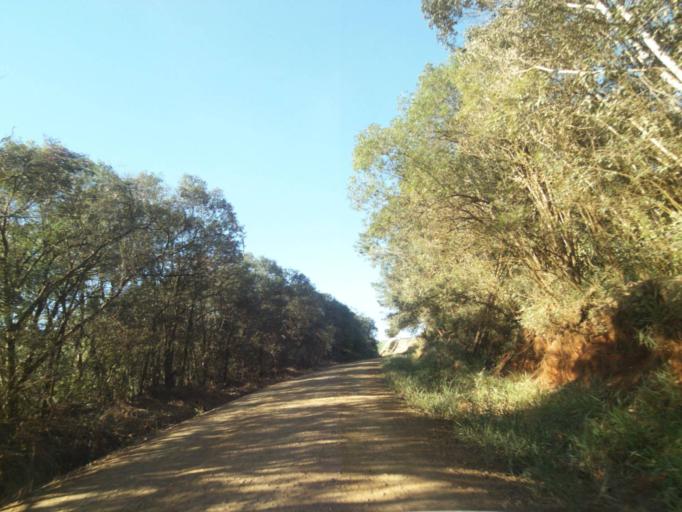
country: BR
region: Parana
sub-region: Tibagi
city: Tibagi
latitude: -24.5307
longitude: -50.4924
